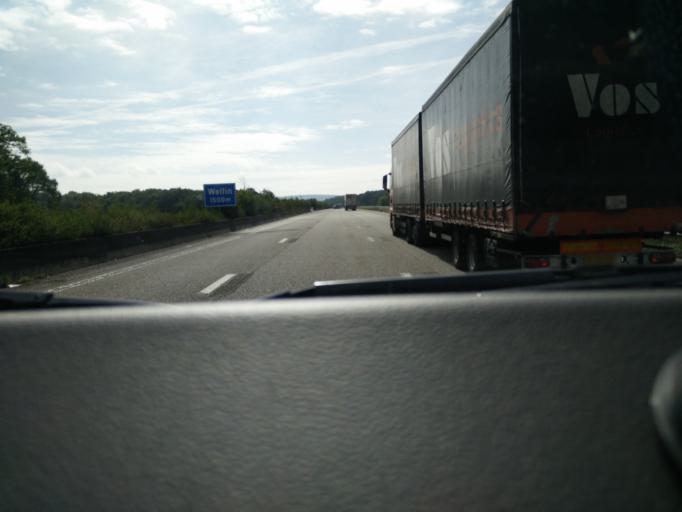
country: BE
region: Wallonia
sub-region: Province du Luxembourg
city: Wellin
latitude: 50.1071
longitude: 5.1153
